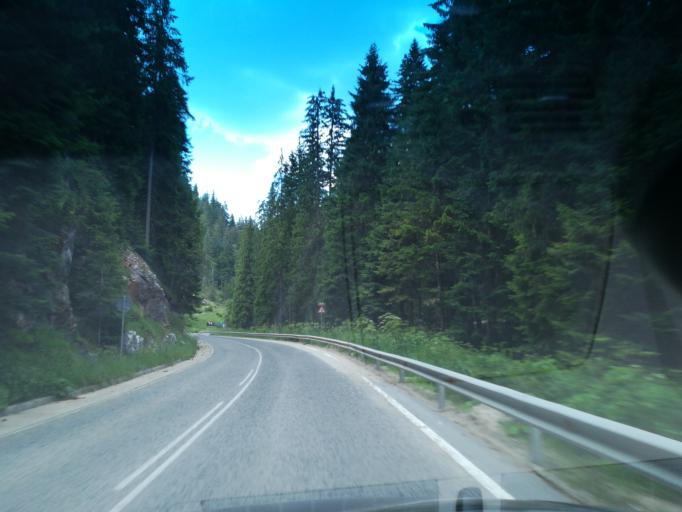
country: BG
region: Smolyan
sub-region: Obshtina Chepelare
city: Chepelare
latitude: 41.6613
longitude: 24.7135
